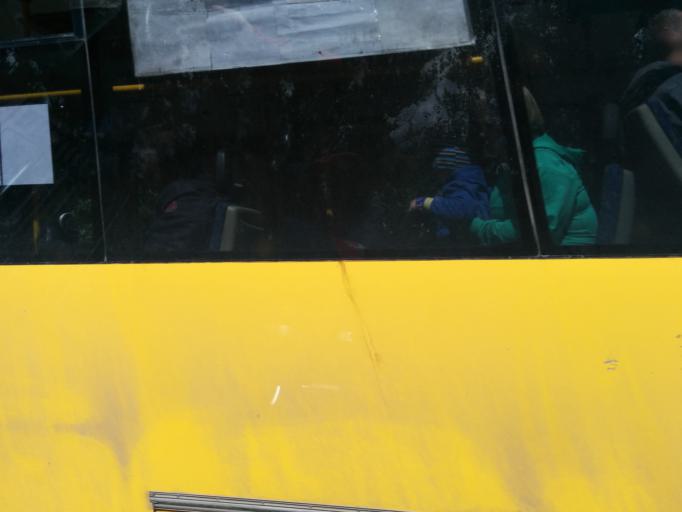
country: RU
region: Perm
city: Kondratovo
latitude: 58.0423
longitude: 56.0484
